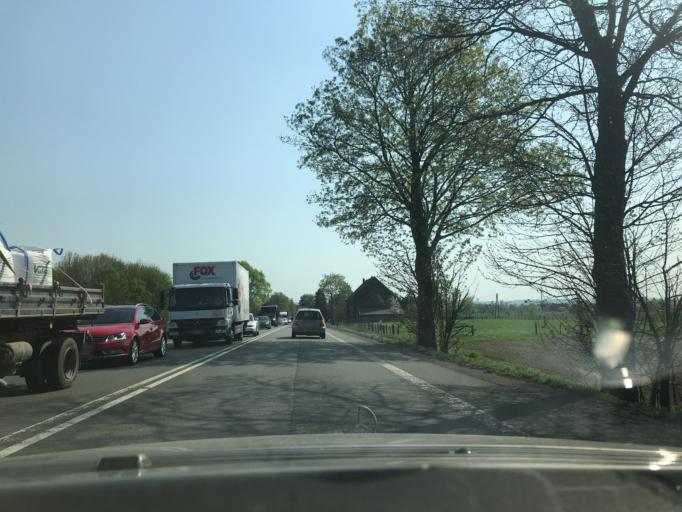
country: DE
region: North Rhine-Westphalia
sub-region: Regierungsbezirk Arnsberg
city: Hamm
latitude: 51.6096
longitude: 7.8519
